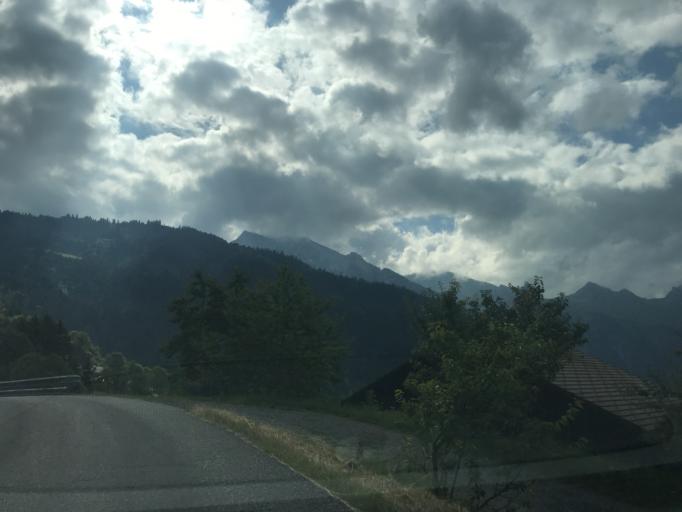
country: FR
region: Rhone-Alpes
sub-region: Departement de la Haute-Savoie
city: La Clusaz
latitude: 45.8686
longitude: 6.3841
